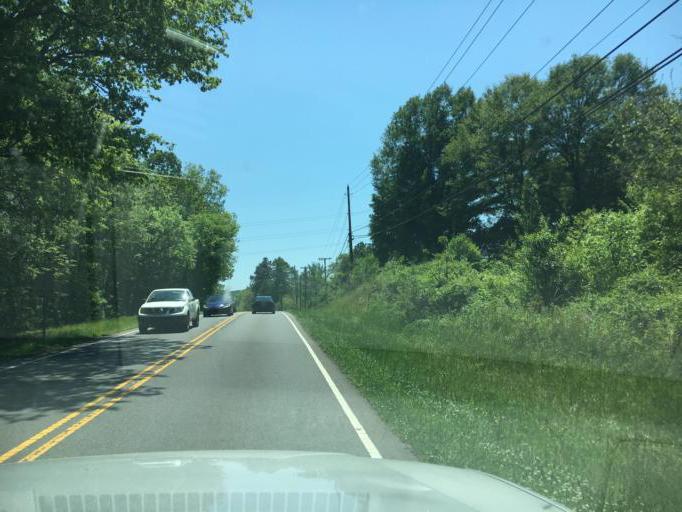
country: US
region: North Carolina
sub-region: Cleveland County
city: Shelby
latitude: 35.2469
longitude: -81.5667
